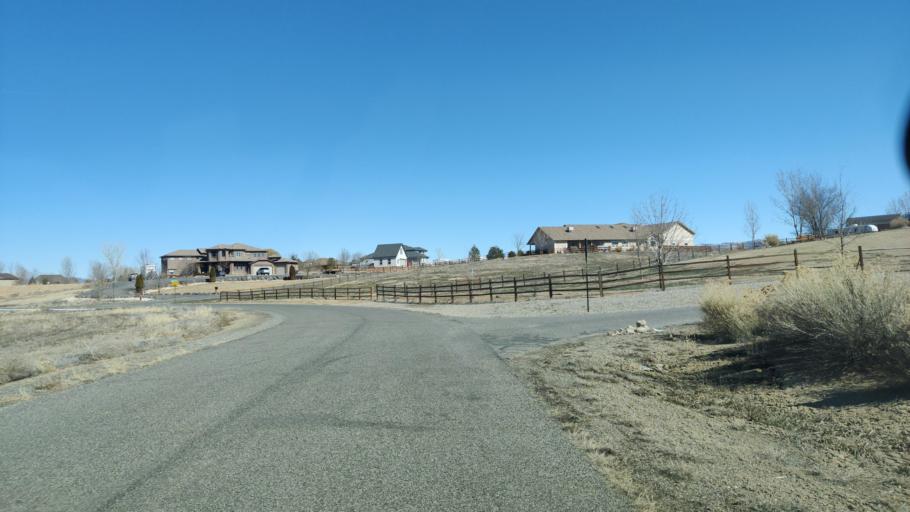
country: US
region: Colorado
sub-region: Mesa County
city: Fruita
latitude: 39.2065
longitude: -108.7081
